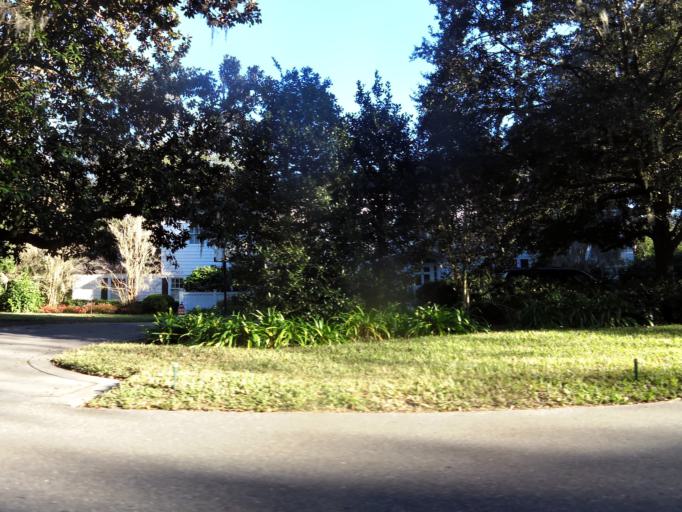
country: US
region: Florida
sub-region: Duval County
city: Jacksonville
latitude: 30.2805
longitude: -81.7008
